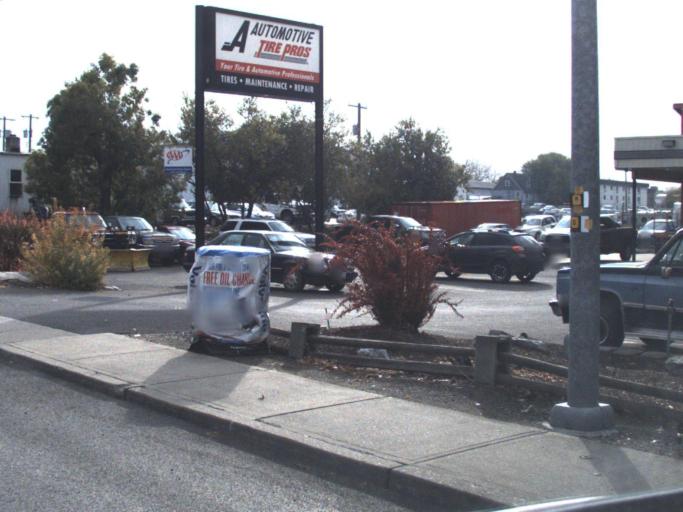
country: US
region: Washington
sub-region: Stevens County
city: Colville
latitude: 48.5487
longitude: -117.9092
